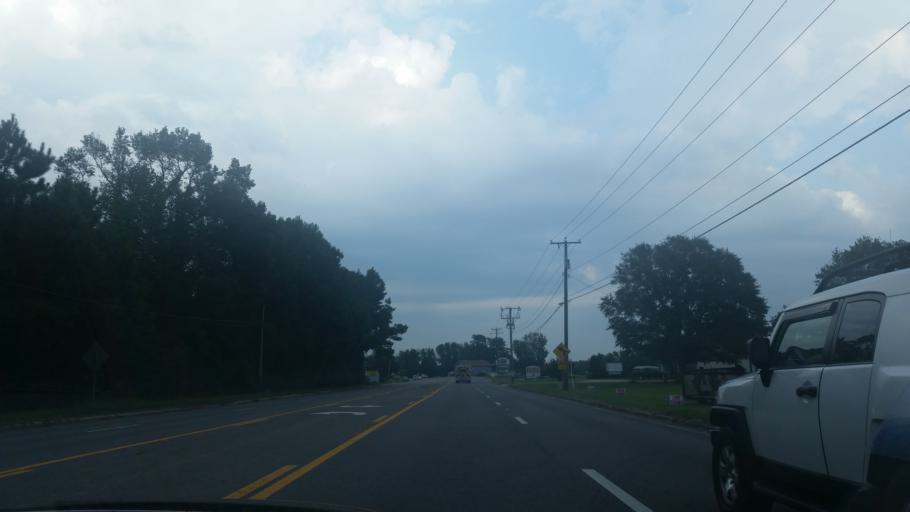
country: US
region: North Carolina
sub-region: Dare County
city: Southern Shores
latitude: 36.2457
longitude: -75.8855
